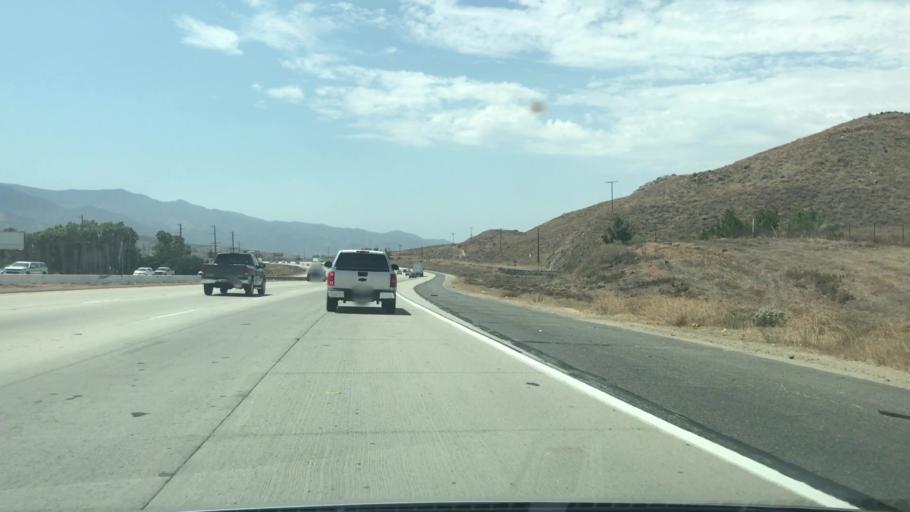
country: US
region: California
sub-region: Riverside County
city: Lake Elsinore
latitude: 33.7311
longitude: -117.3996
